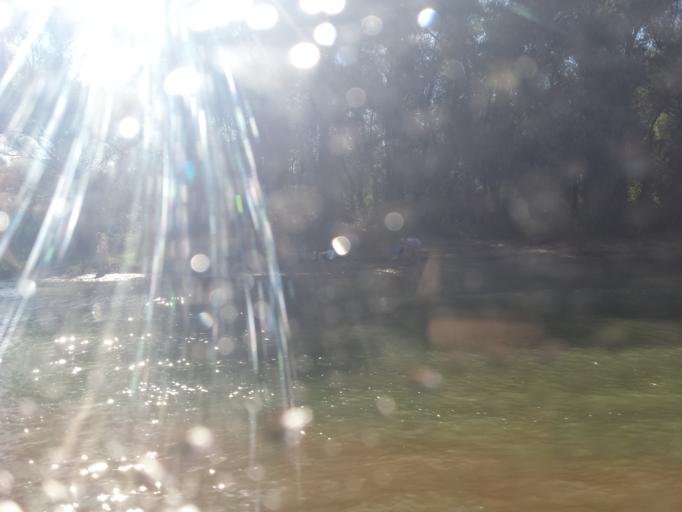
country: RO
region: Tulcea
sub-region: Municipiul Tulcea
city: Tulcea
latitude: 45.2113
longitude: 28.8613
